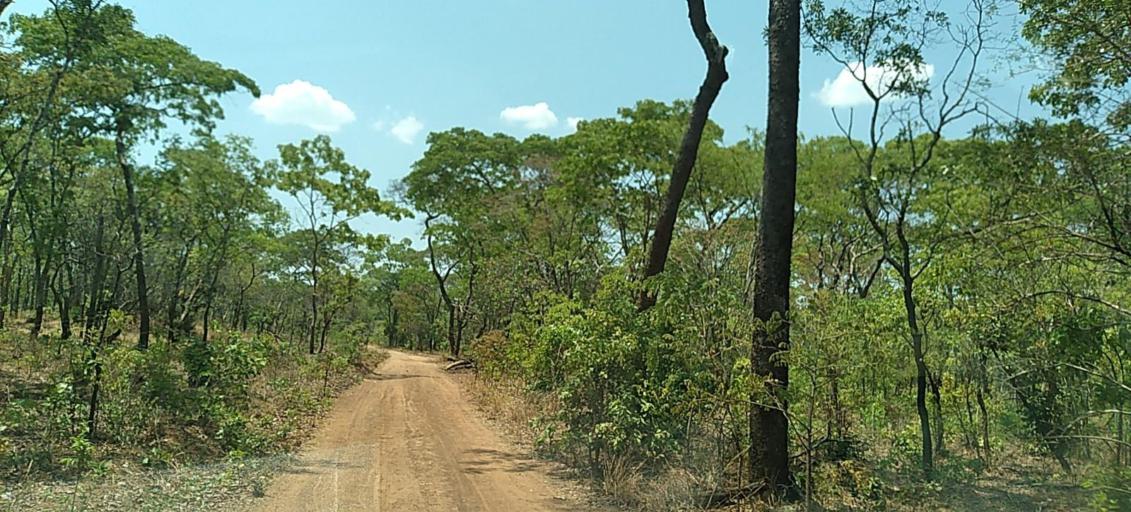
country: ZM
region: Copperbelt
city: Mpongwe
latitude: -13.6475
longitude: 28.4859
